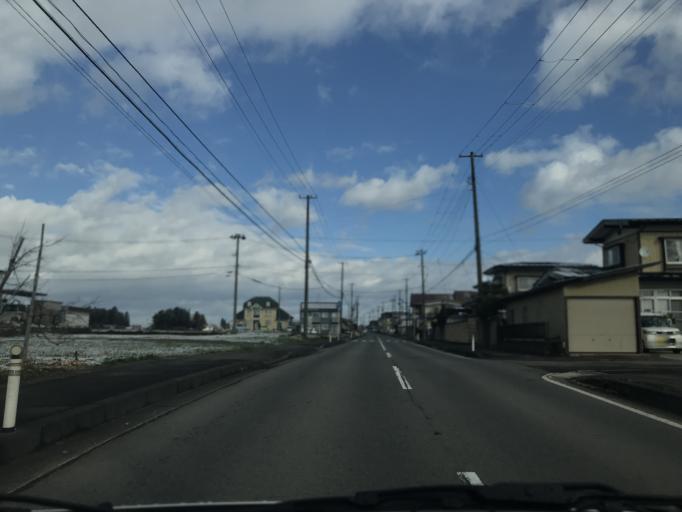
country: JP
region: Iwate
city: Mizusawa
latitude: 39.1104
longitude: 141.1364
